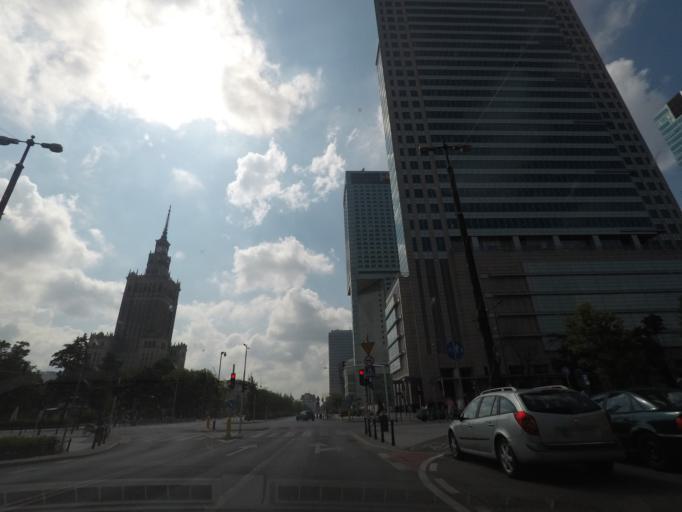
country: PL
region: Masovian Voivodeship
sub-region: Warszawa
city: Warsaw
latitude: 52.2343
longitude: 21.0020
